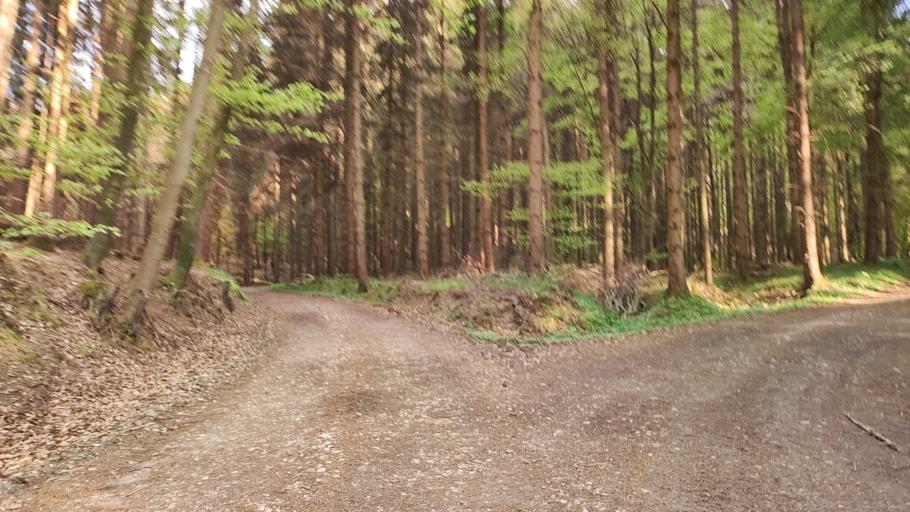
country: DE
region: Bavaria
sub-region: Swabia
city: Zusmarshausen
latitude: 48.4032
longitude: 10.6199
